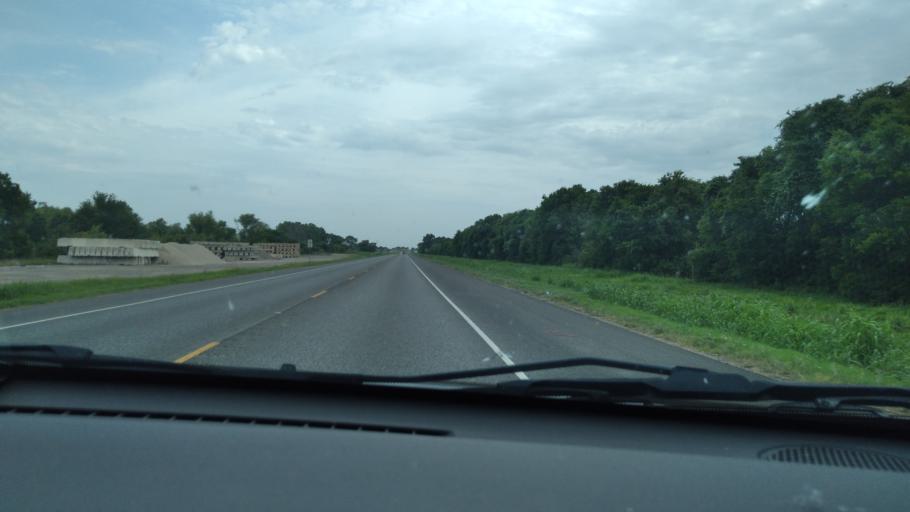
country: US
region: Texas
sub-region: McLennan County
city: Bellmead
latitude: 31.5607
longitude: -97.0679
